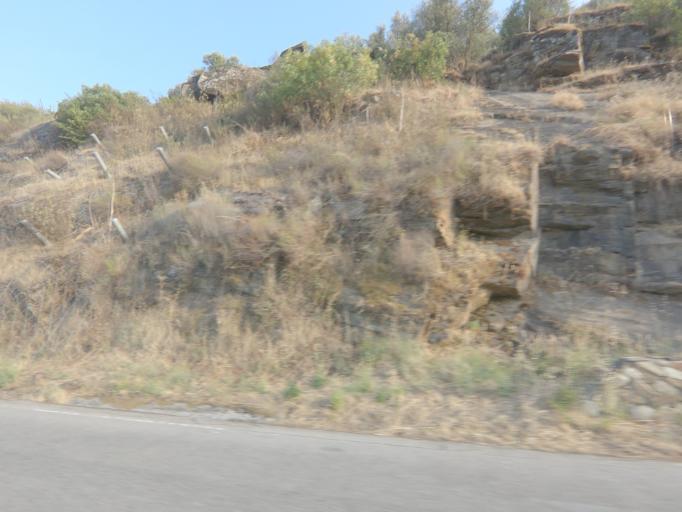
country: PT
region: Viseu
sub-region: Armamar
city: Armamar
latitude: 41.1443
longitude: -7.7290
